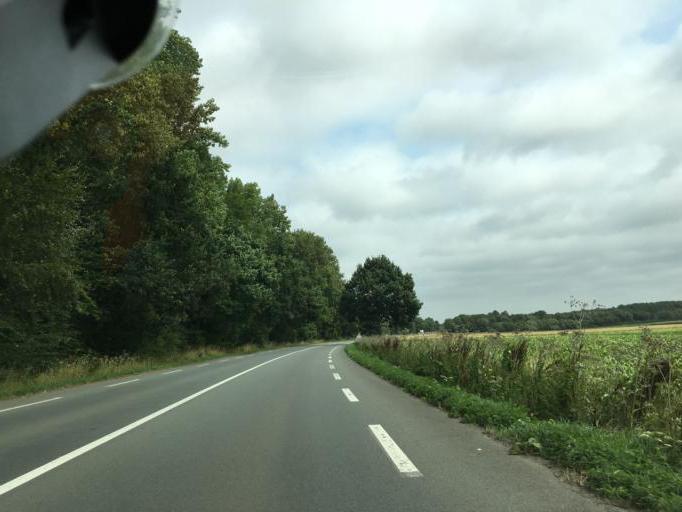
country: FR
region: Nord-Pas-de-Calais
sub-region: Departement du Pas-de-Calais
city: Pernes
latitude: 50.4224
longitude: 2.4244
